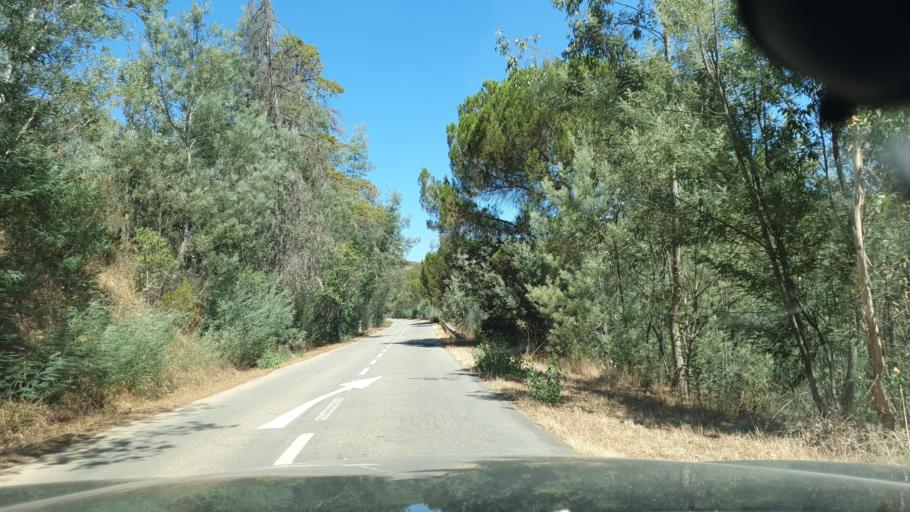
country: PT
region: Beja
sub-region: Odemira
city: Odemira
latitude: 37.5086
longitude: -8.4610
